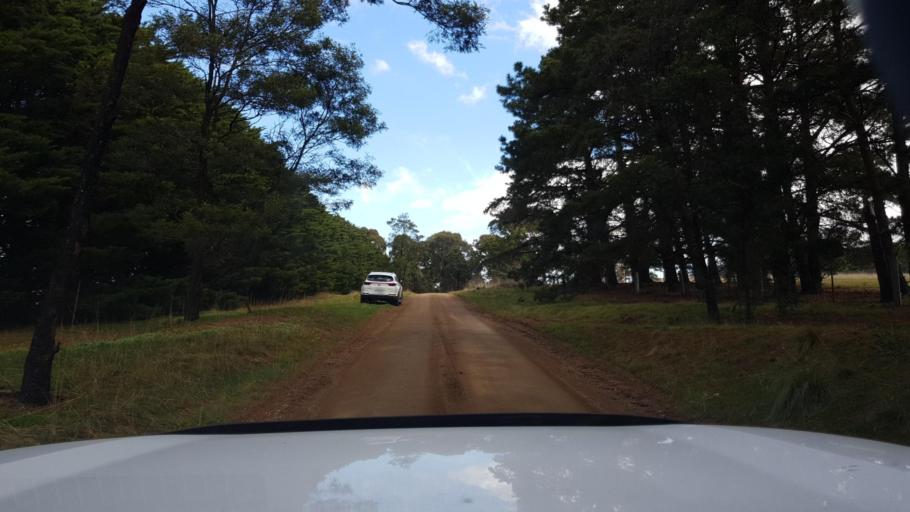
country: AU
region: Victoria
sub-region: Hume
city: Sunbury
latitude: -37.5638
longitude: 144.6211
